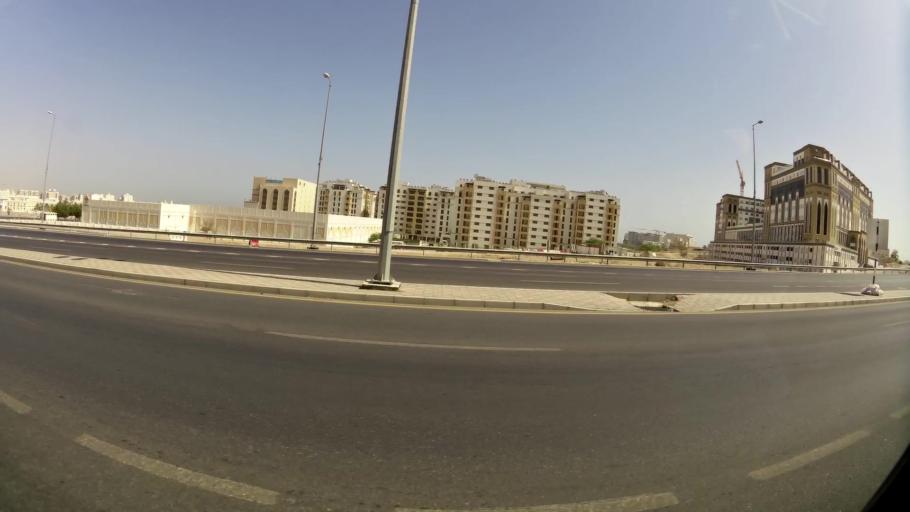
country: OM
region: Muhafazat Masqat
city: Bawshar
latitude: 23.5774
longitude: 58.4101
